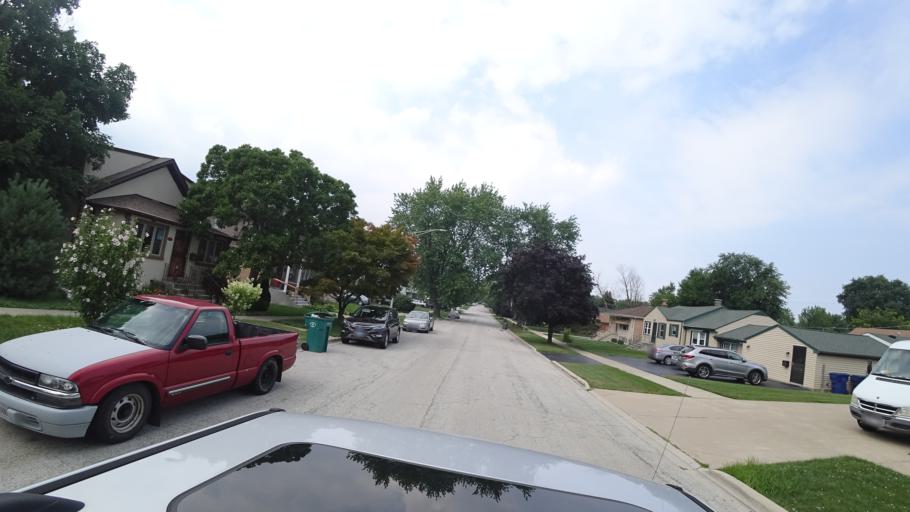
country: US
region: Illinois
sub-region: Cook County
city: Chicago Ridge
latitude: 41.6986
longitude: -87.7767
